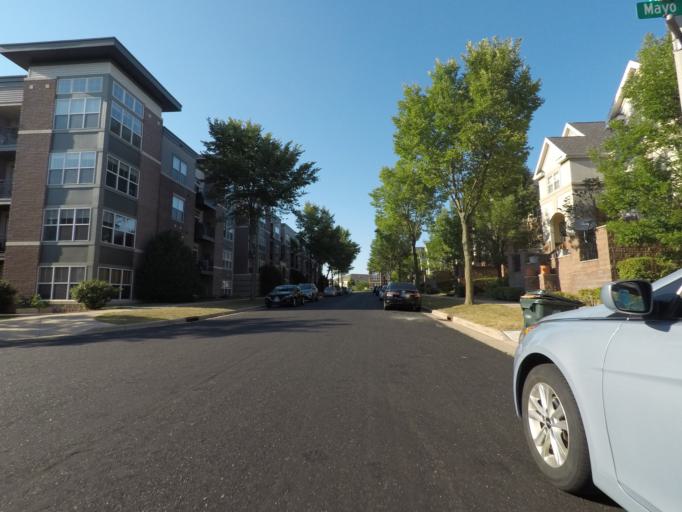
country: US
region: Wisconsin
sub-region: Dane County
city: Verona
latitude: 43.0328
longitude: -89.5238
